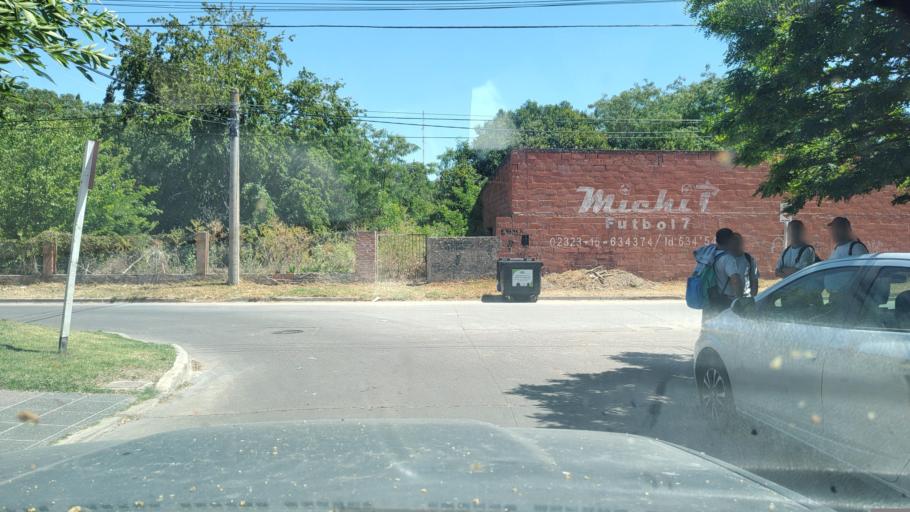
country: AR
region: Buenos Aires
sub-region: Partido de Lujan
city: Lujan
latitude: -34.5836
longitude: -59.1134
